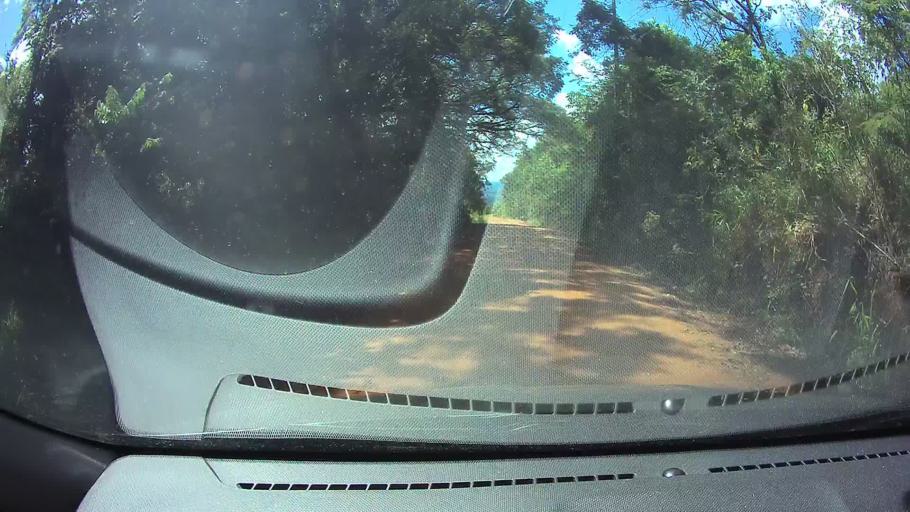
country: PY
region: Paraguari
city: La Colmena
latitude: -25.9409
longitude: -56.7793
